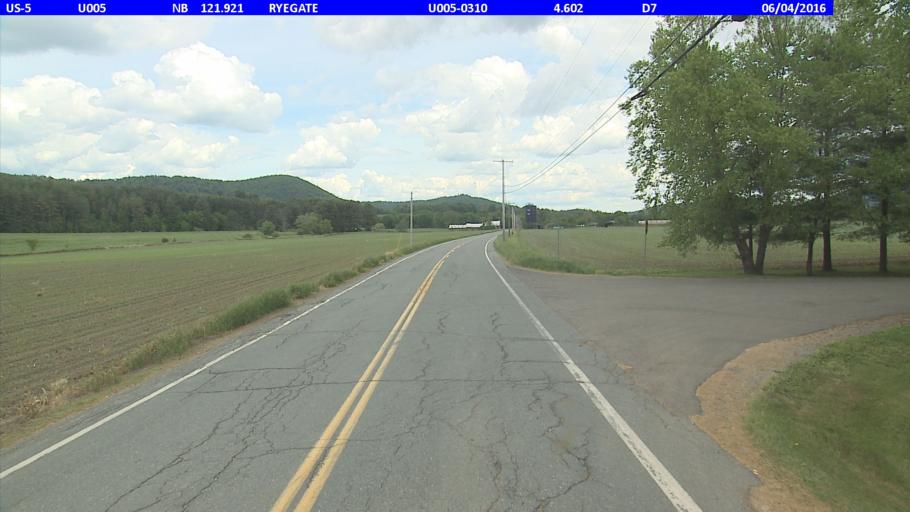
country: US
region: New Hampshire
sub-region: Grafton County
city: Woodsville
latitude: 44.2179
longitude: -72.0590
